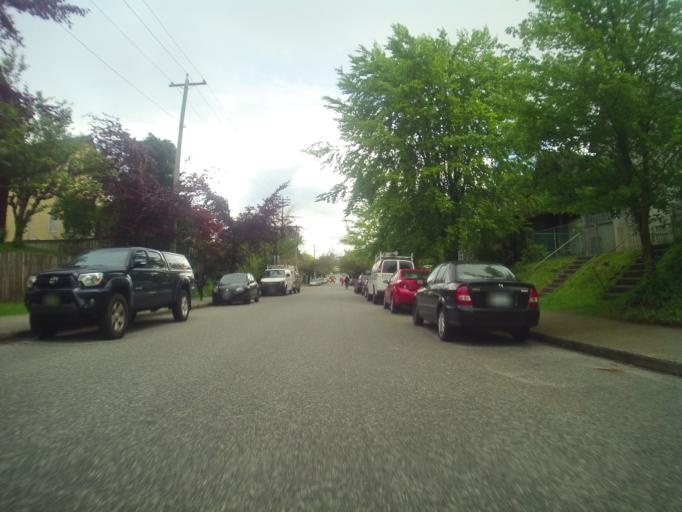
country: CA
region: British Columbia
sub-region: Fraser Valley Regional District
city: North Vancouver
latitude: 49.2774
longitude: -123.0859
